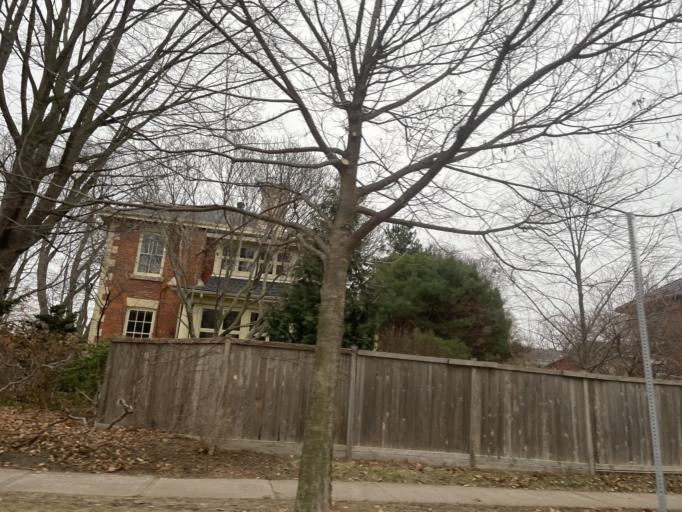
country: CA
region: Ontario
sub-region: Wellington County
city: Guelph
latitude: 43.5464
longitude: -80.2561
